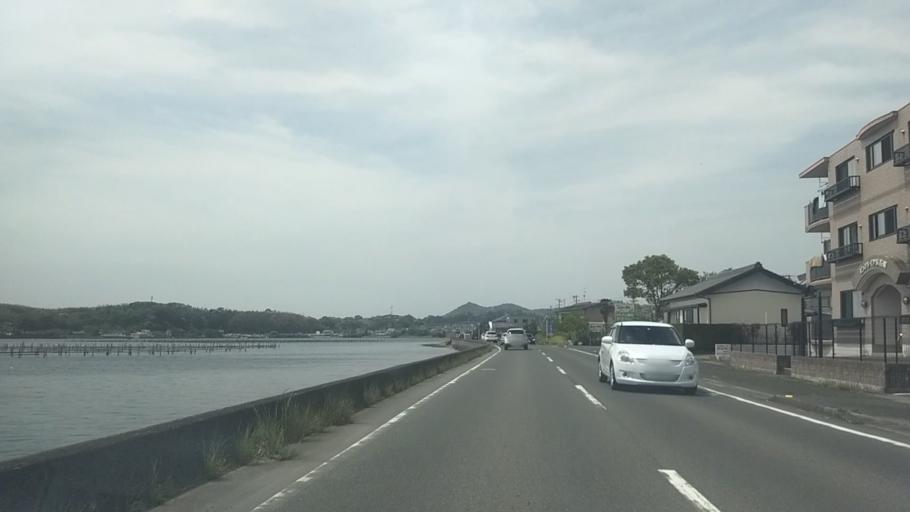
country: JP
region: Shizuoka
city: Kosai-shi
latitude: 34.7616
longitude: 137.5206
